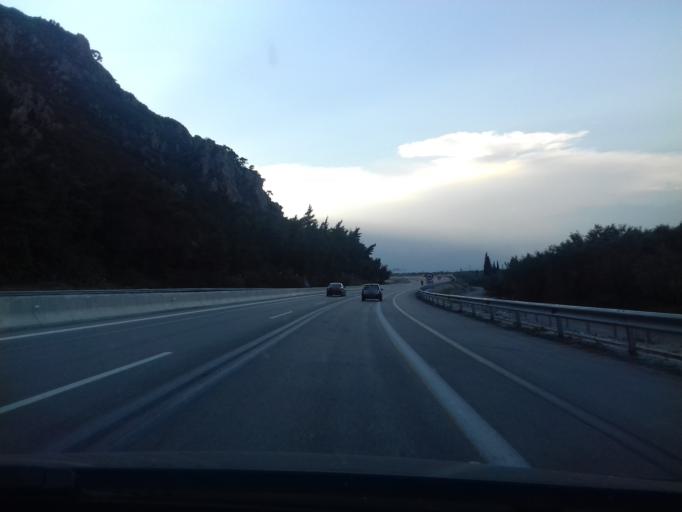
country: GR
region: West Greece
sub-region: Nomos Achaias
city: Temeni
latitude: 38.1869
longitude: 22.1776
